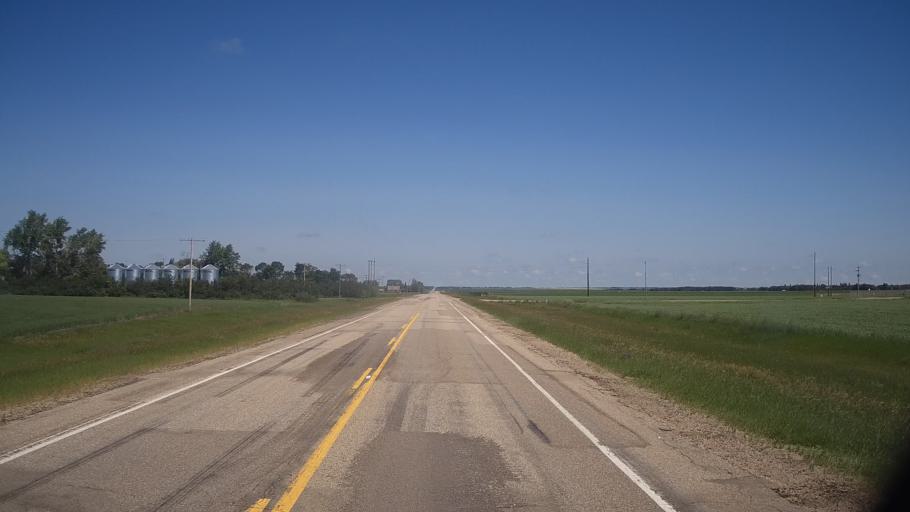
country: CA
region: Saskatchewan
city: Saskatoon
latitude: 51.9798
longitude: -106.0754
